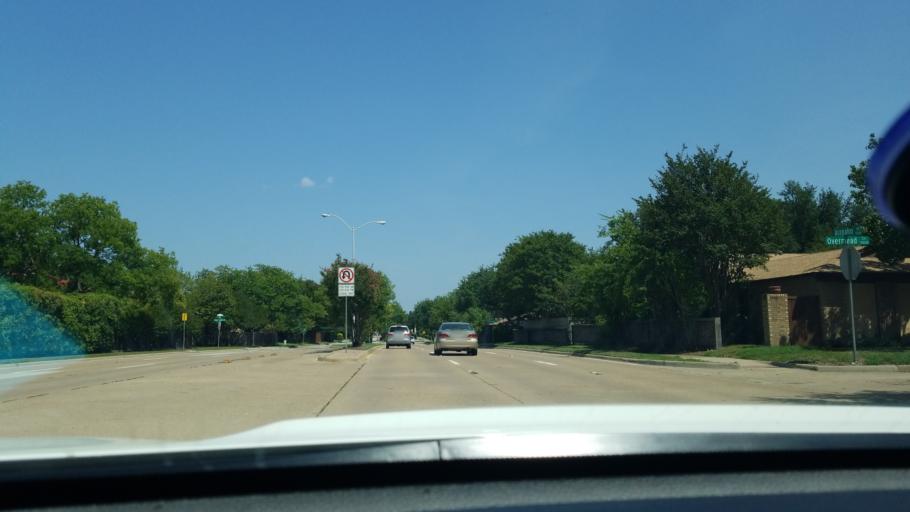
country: US
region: Texas
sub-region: Dallas County
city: Addison
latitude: 32.9620
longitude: -96.7830
